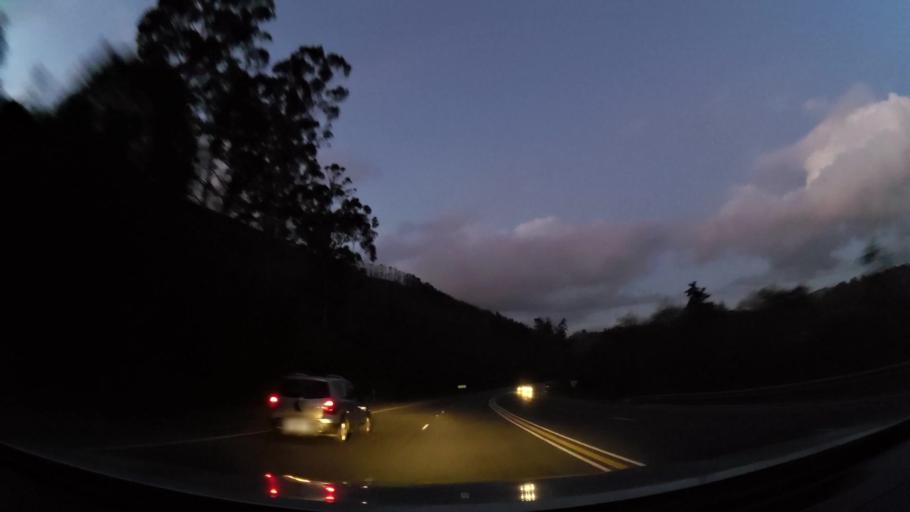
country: ZA
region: Western Cape
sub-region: Eden District Municipality
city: Knysna
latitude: -34.0373
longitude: 22.9268
